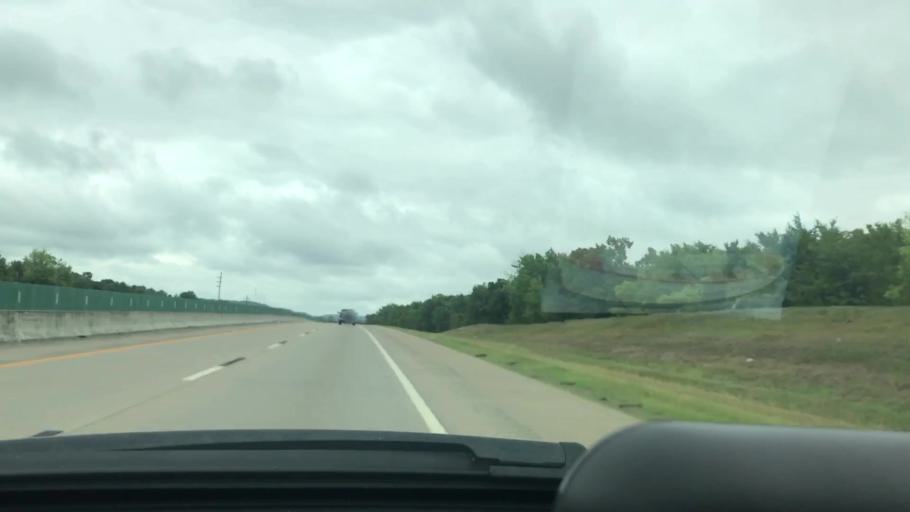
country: US
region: Oklahoma
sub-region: Pittsburg County
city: Krebs
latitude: 35.0330
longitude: -95.7130
